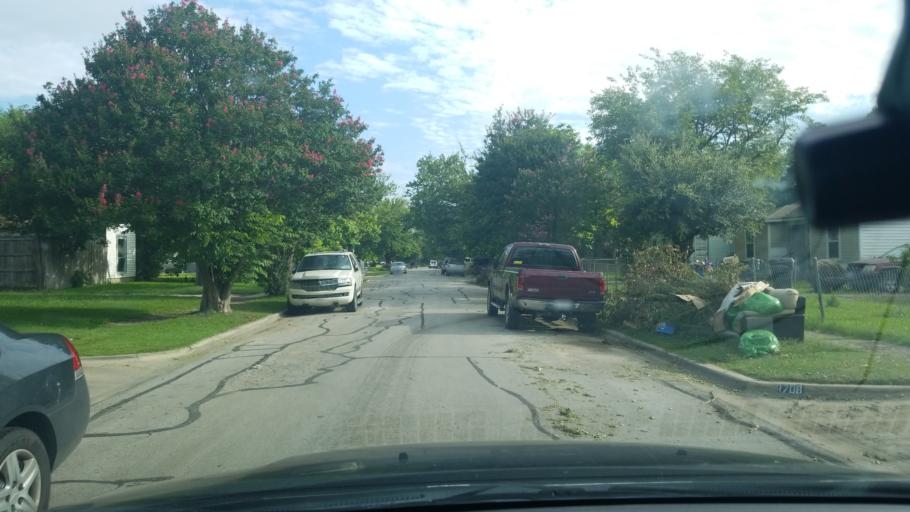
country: US
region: Texas
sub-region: Dallas County
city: Balch Springs
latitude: 32.7408
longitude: -96.6704
